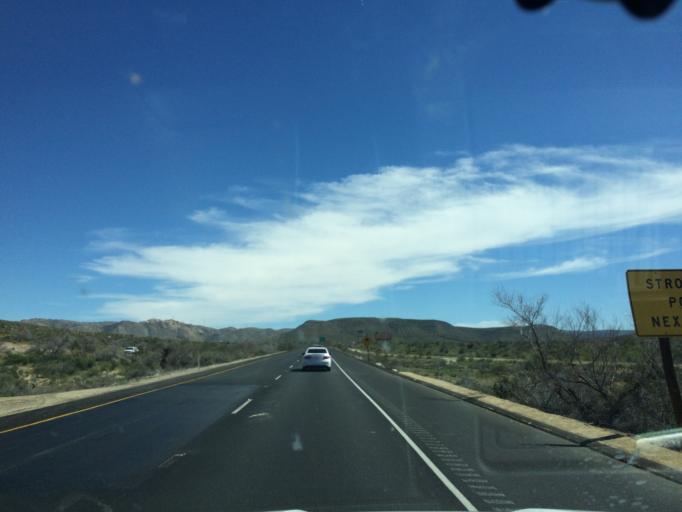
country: MX
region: Baja California
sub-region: Tecate
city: Cereso del Hongo
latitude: 32.6394
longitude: -116.1718
